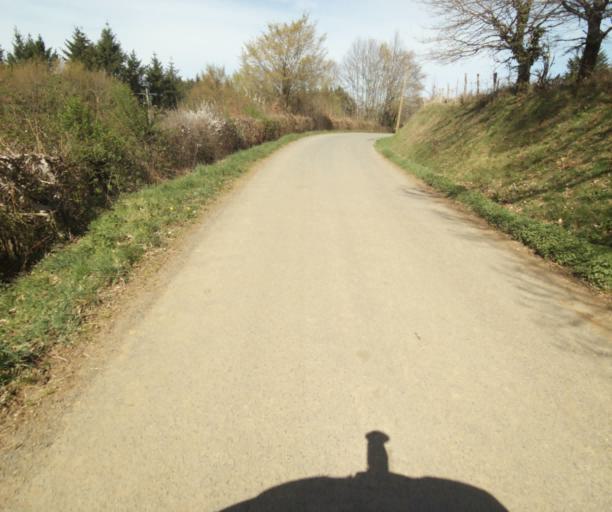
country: FR
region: Limousin
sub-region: Departement de la Correze
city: Seilhac
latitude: 45.3909
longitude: 1.7814
